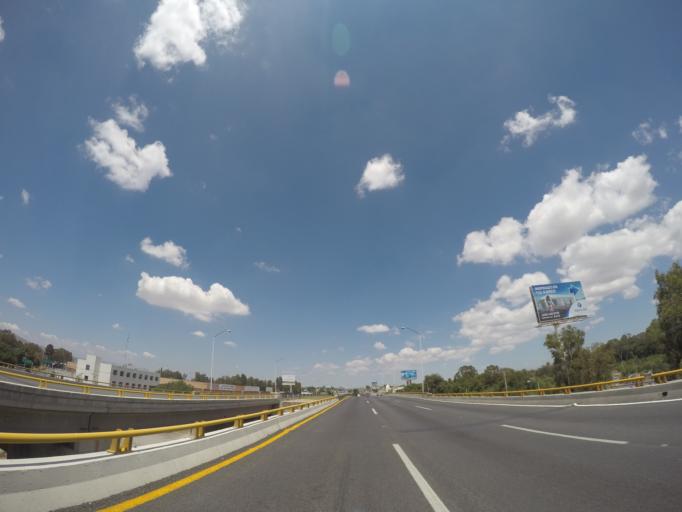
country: MX
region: San Luis Potosi
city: La Pila
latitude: 22.0833
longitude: -100.8779
